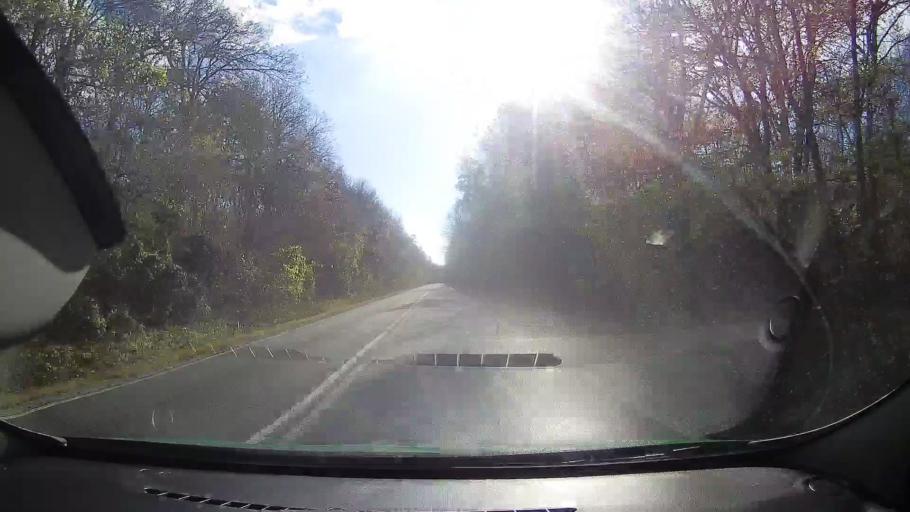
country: RO
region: Tulcea
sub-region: Oras Babadag
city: Babadag
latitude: 44.8487
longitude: 28.6983
